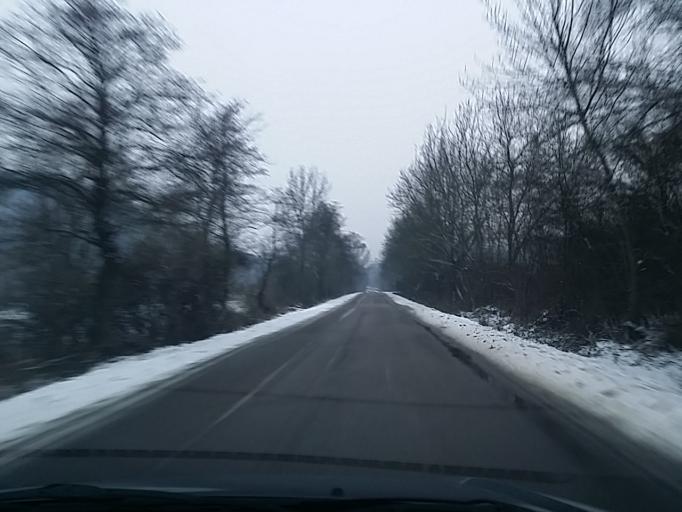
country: HU
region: Heves
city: Sirok
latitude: 47.9116
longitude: 20.1780
